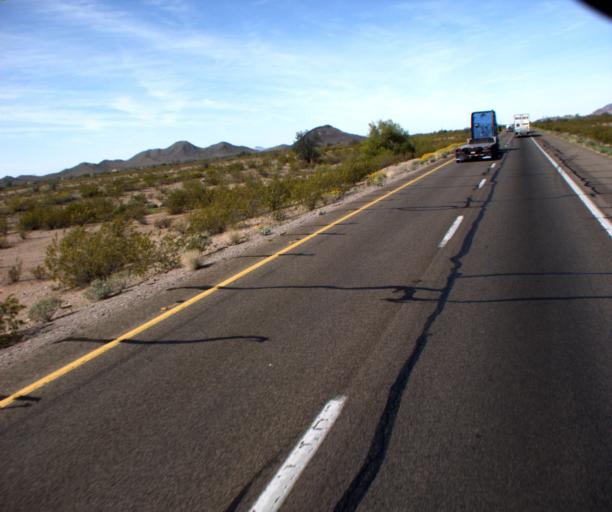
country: US
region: Arizona
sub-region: Maricopa County
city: Buckeye
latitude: 33.5065
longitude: -112.9849
